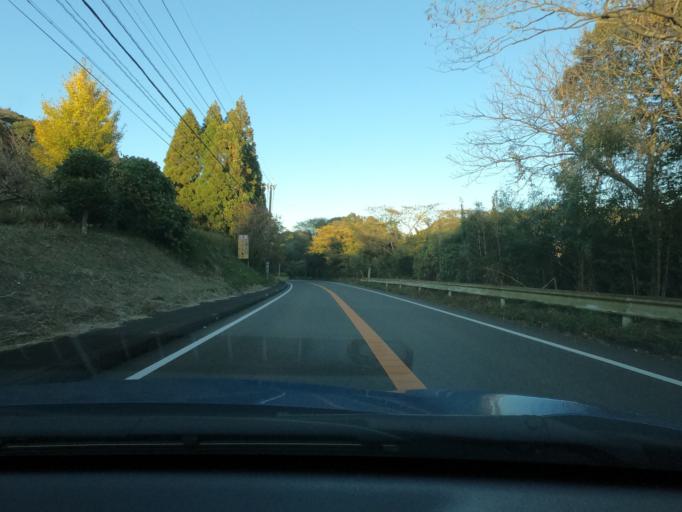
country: JP
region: Kagoshima
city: Satsumasendai
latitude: 31.8107
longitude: 130.3703
